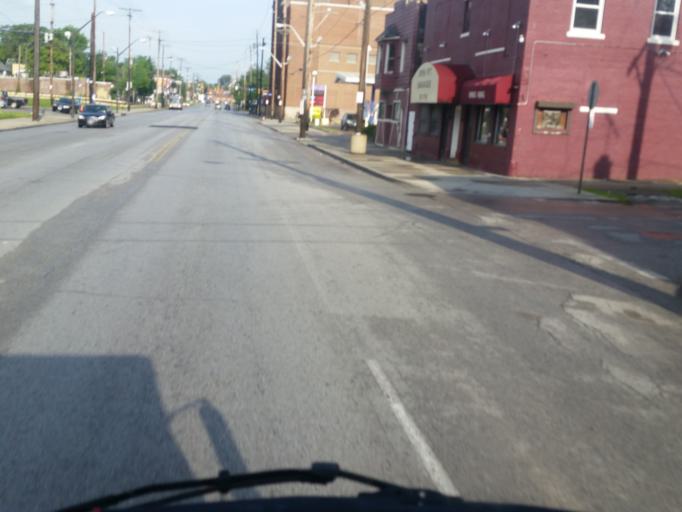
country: US
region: Ohio
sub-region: Cuyahoga County
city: East Cleveland
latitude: 41.5414
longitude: -81.5986
